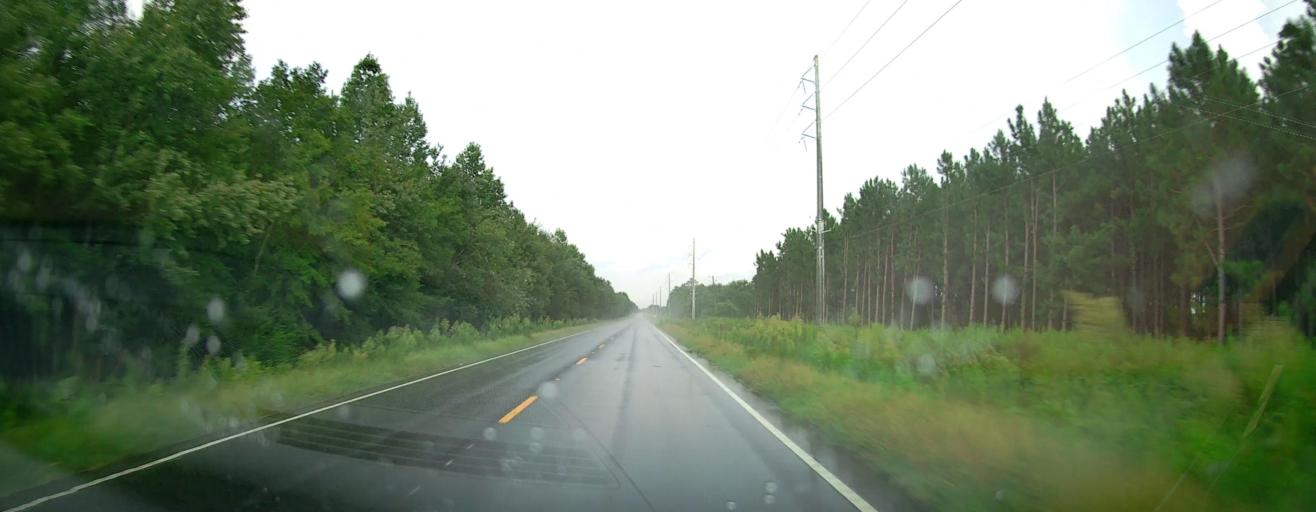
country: US
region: Georgia
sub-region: Dodge County
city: Chester
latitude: 32.5670
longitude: -83.1770
